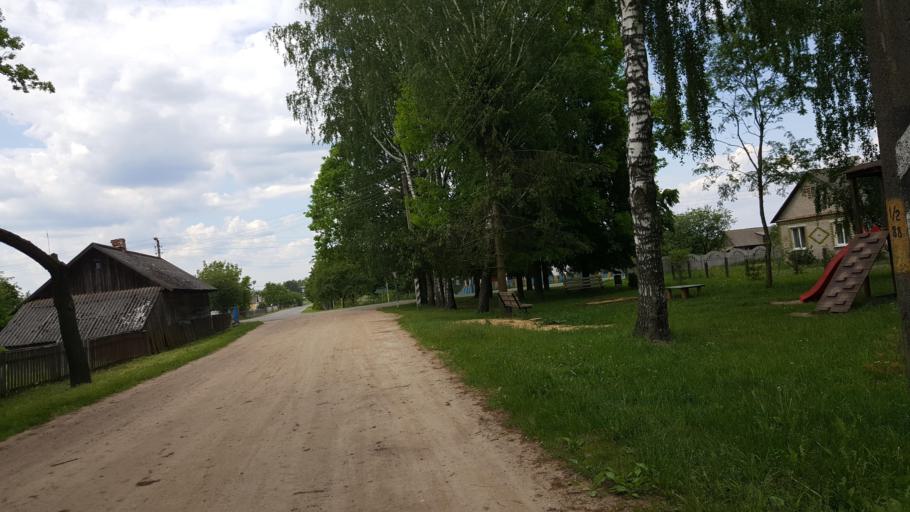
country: PL
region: Podlasie
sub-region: Powiat hajnowski
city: Bialowieza
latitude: 52.6703
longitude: 24.0847
